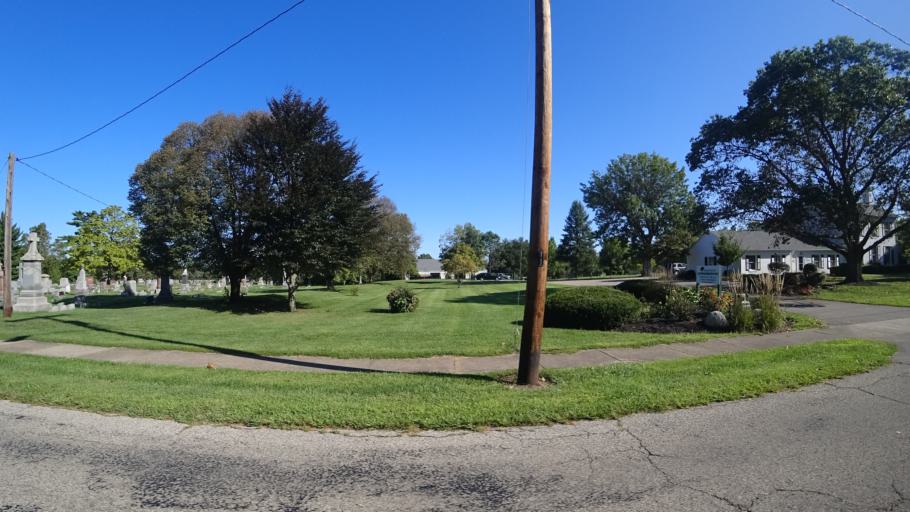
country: US
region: Ohio
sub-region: Butler County
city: Hamilton
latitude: 39.4056
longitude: -84.5408
